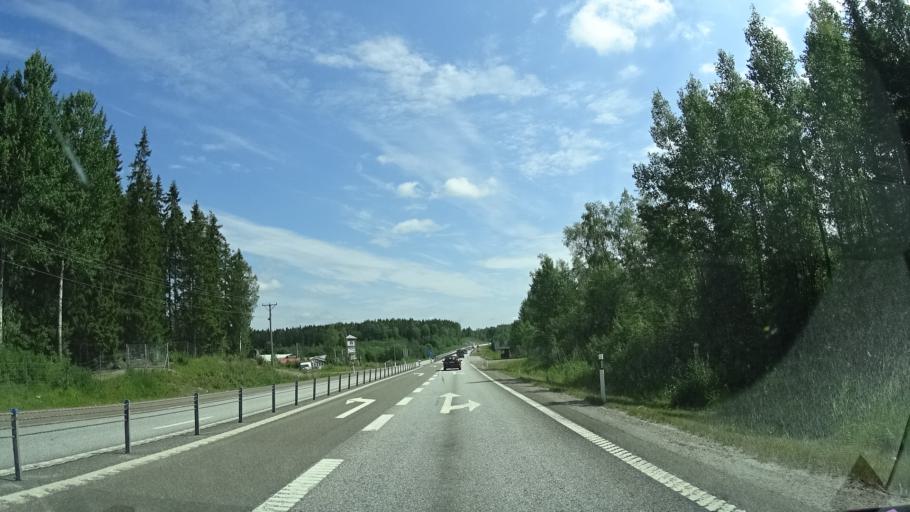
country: SE
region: OErebro
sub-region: Degerfors Kommun
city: Degerfors
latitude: 59.3240
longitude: 14.3679
